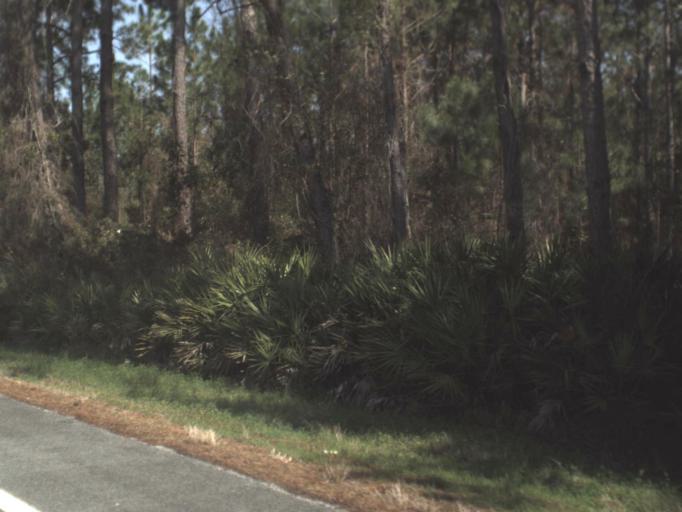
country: US
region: Florida
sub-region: Franklin County
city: Carrabelle
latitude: 29.9333
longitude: -84.5091
